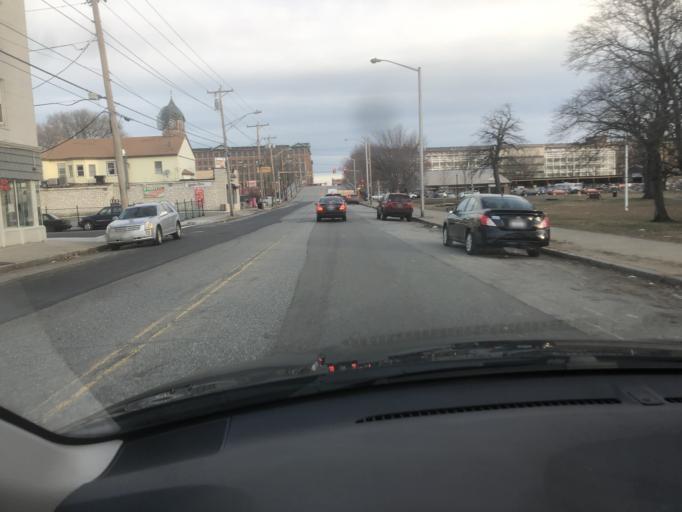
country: US
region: Massachusetts
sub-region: Essex County
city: Lawrence
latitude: 42.6996
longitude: -71.1534
